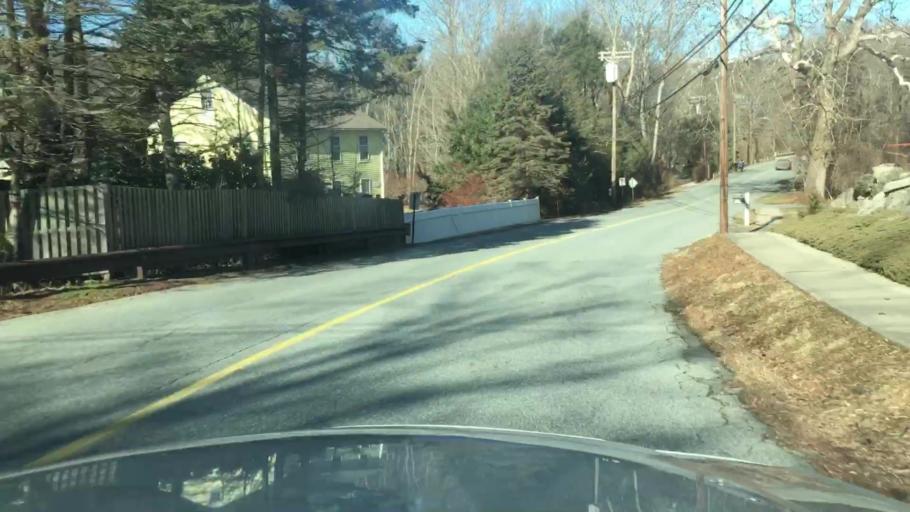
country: US
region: Connecticut
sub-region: Middlesex County
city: Essex Village
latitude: 41.3621
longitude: -72.4010
